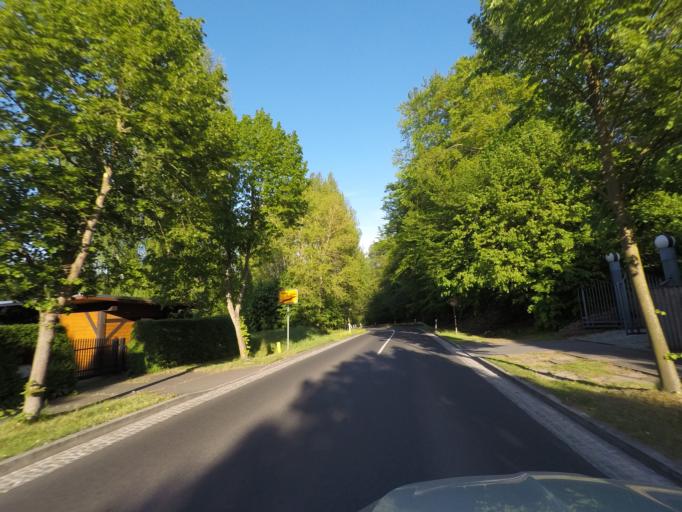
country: DE
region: Brandenburg
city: Falkenberg
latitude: 52.8001
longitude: 13.9687
